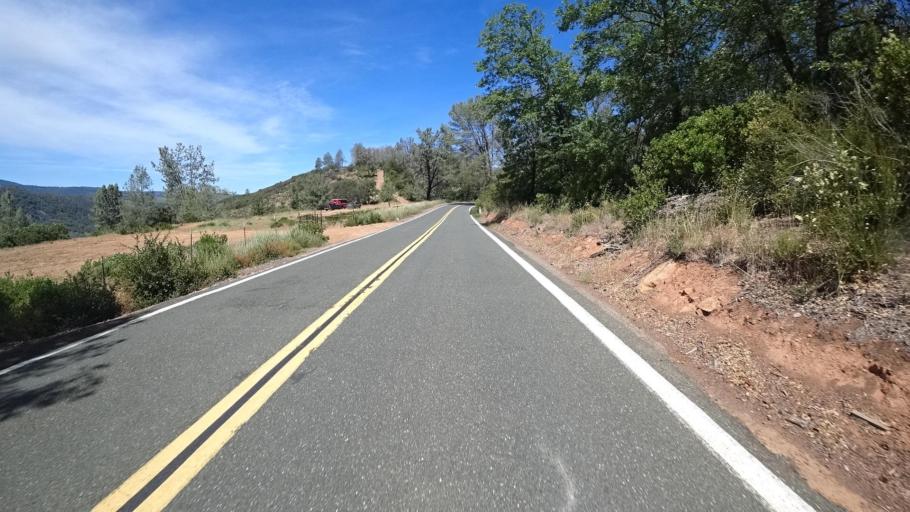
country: US
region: California
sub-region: Lake County
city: Clearlake
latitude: 38.9361
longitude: -122.6642
